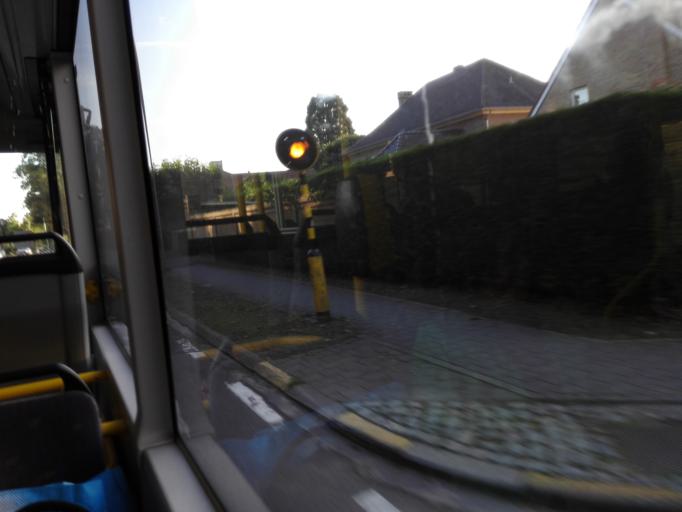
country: BE
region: Flanders
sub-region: Provincie Vlaams-Brabant
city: Wezembeek-Oppem
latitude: 50.8433
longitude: 4.4984
